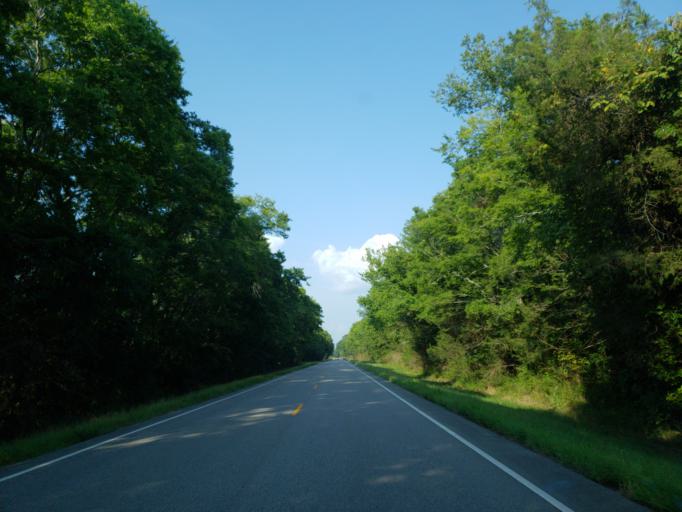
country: US
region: Alabama
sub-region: Greene County
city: Eutaw
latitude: 32.7480
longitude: -88.0424
